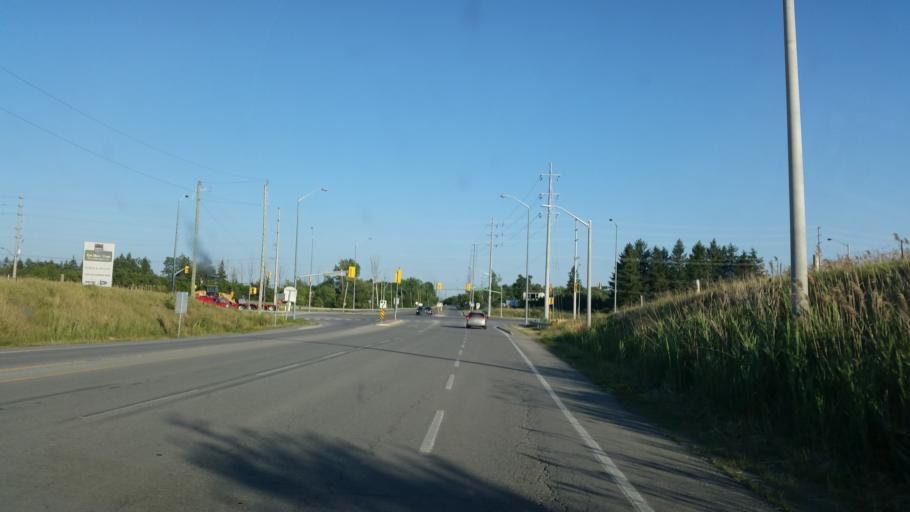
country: CA
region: Ontario
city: Brampton
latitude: 43.7535
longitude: -79.8043
